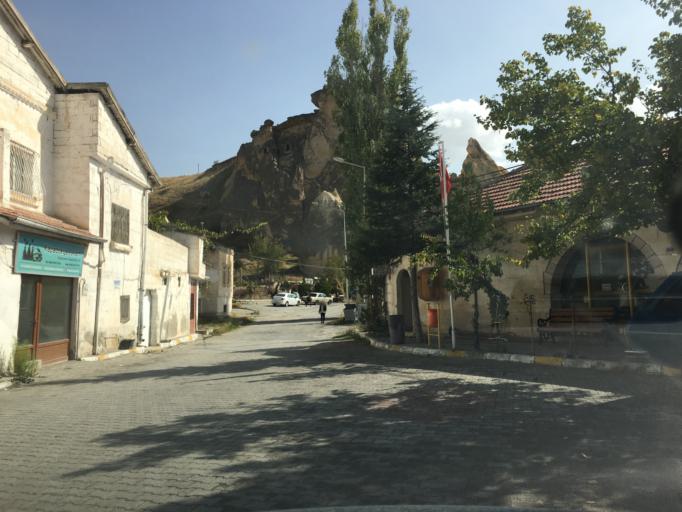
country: TR
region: Nevsehir
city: Goereme
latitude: 38.6689
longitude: 34.8414
